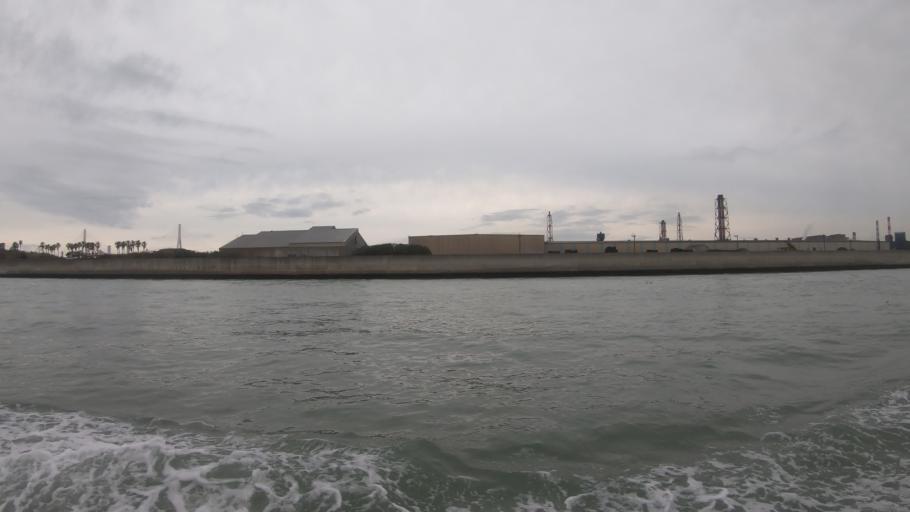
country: JP
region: Kanagawa
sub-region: Kawasaki-shi
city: Kawasaki
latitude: 35.4664
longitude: 139.7202
